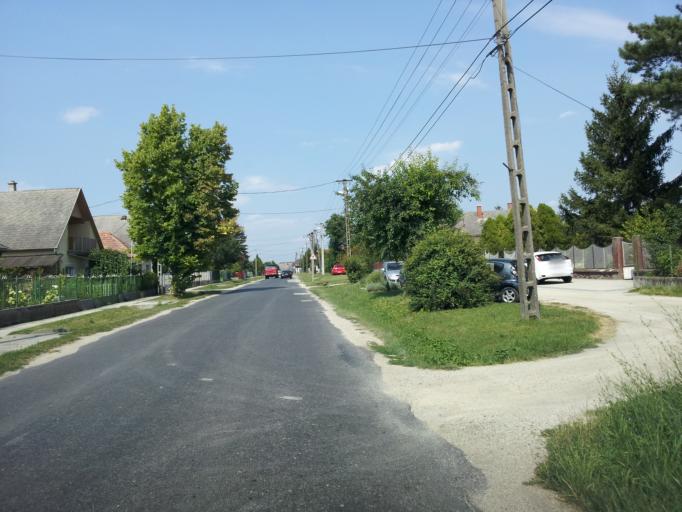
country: HU
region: Veszprem
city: Balatonkenese
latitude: 47.0798
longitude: 18.0786
